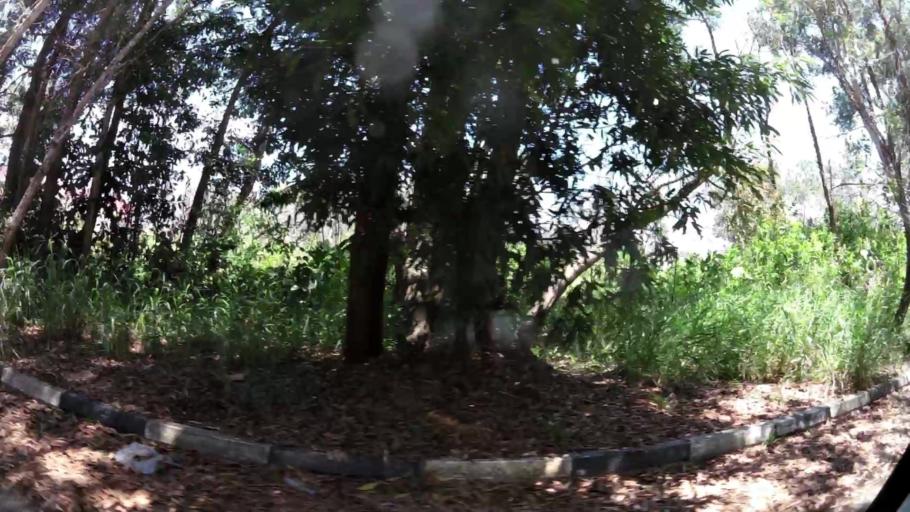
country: BN
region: Brunei and Muara
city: Bandar Seri Begawan
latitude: 4.9235
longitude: 114.9673
